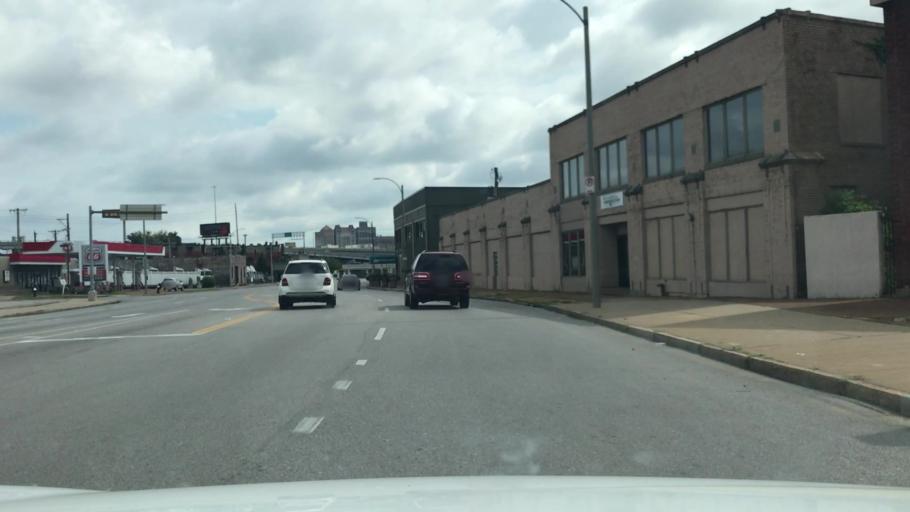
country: US
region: Missouri
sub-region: City of Saint Louis
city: St. Louis
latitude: 38.6291
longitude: -90.2463
